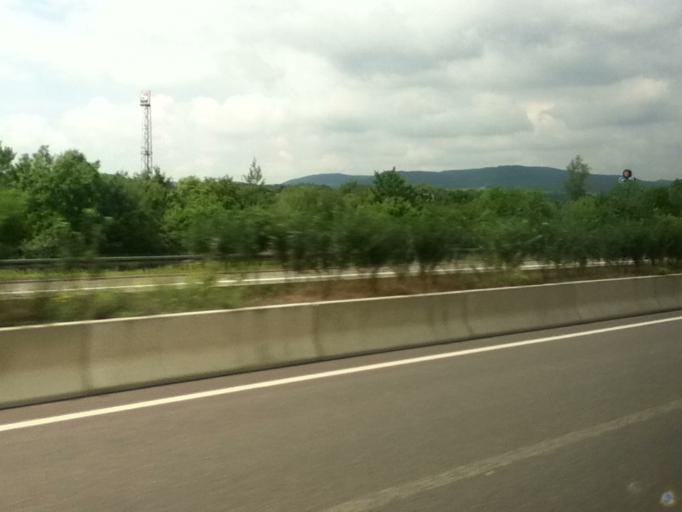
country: DE
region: Thuringia
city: Zollnitz
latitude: 50.8774
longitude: 11.6352
